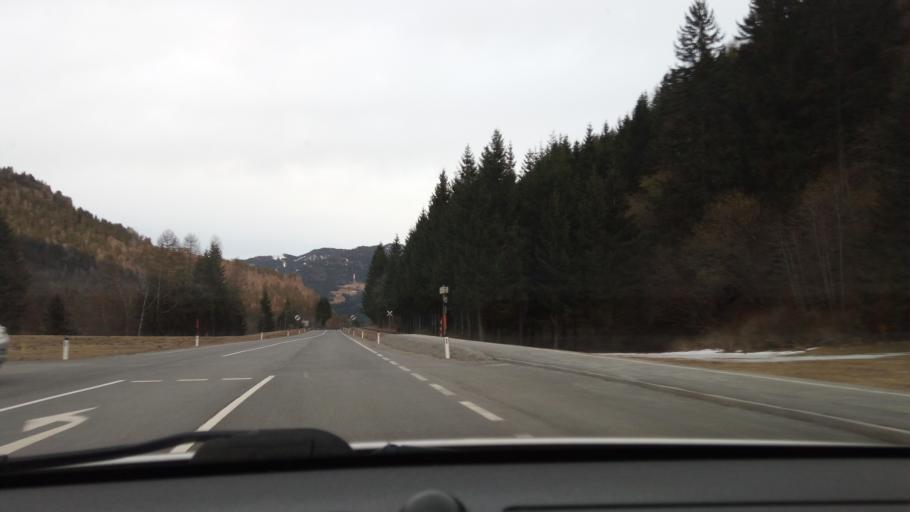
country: AT
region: Styria
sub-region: Politischer Bezirk Murau
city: Stadl an der Mur
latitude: 47.0841
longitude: 13.9403
